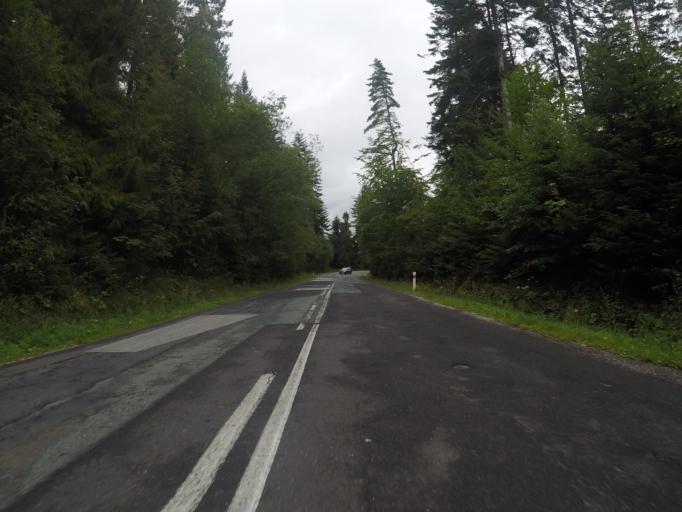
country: SK
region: Kosicky
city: Spisska Nova Ves
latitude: 48.8802
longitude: 20.5321
